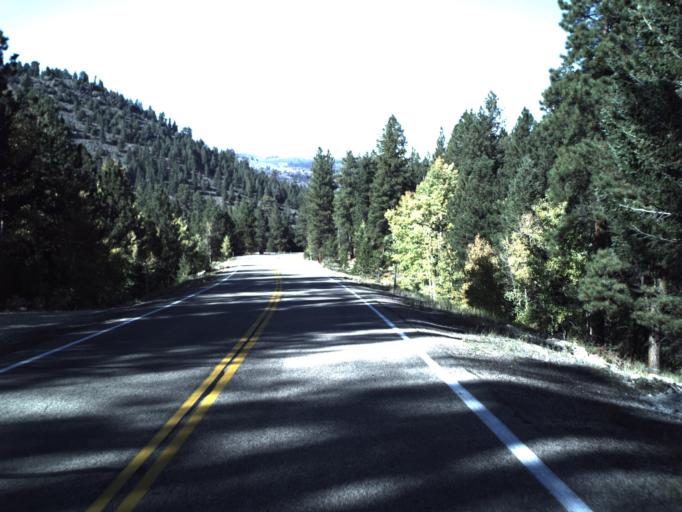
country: US
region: Utah
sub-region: Iron County
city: Parowan
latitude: 37.6929
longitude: -112.6644
